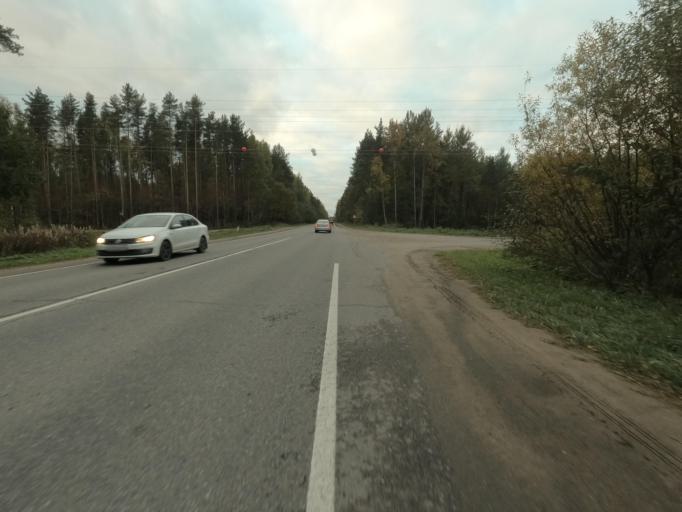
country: RU
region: Leningrad
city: Pavlovo
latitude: 59.8056
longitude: 30.9345
